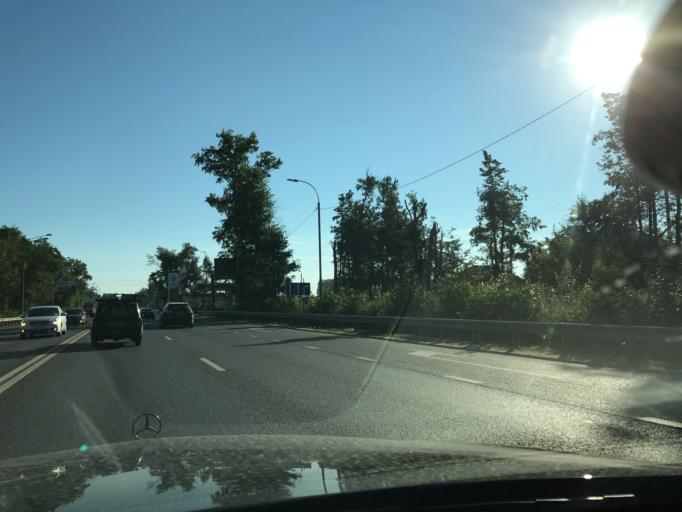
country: RU
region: Moskovskaya
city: Balashikha
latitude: 55.8442
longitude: 37.9559
